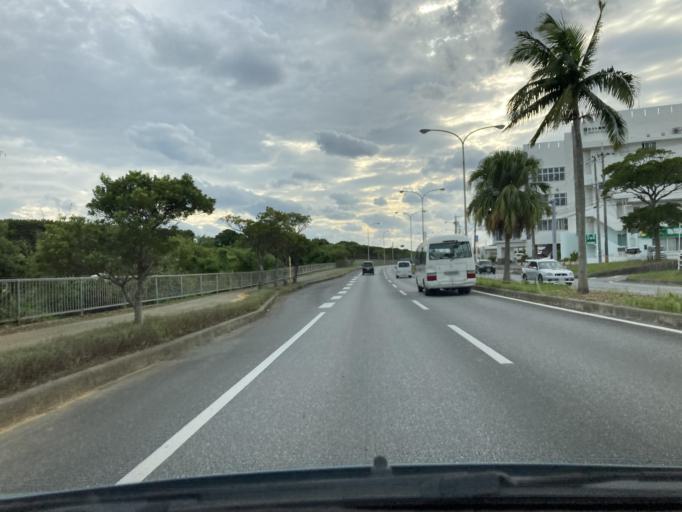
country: JP
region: Okinawa
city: Okinawa
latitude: 26.3674
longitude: 127.7741
